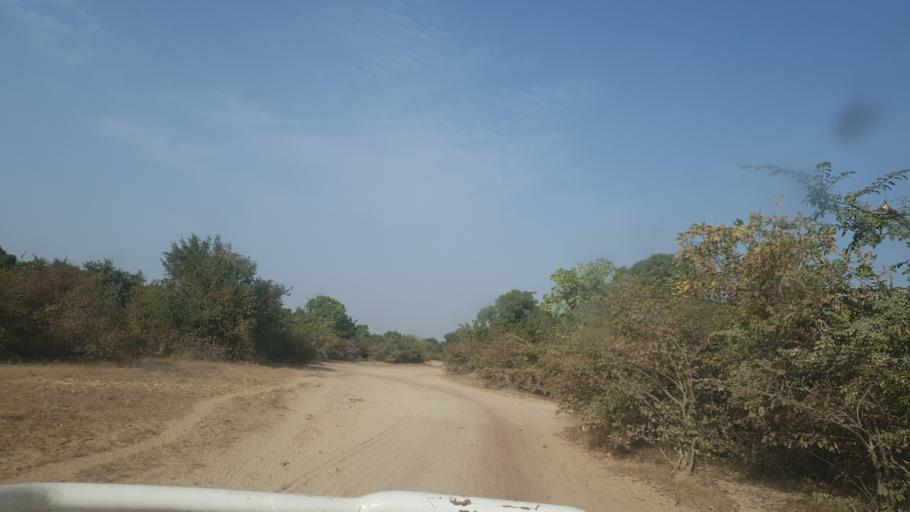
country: ML
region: Segou
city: Baroueli
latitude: 13.3648
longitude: -6.9190
